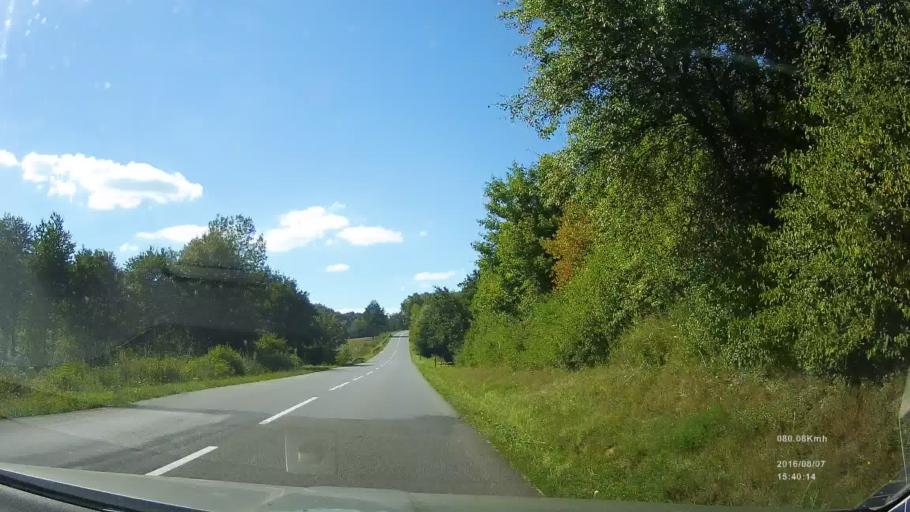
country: SK
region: Presovsky
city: Giraltovce
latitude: 49.1174
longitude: 21.5935
